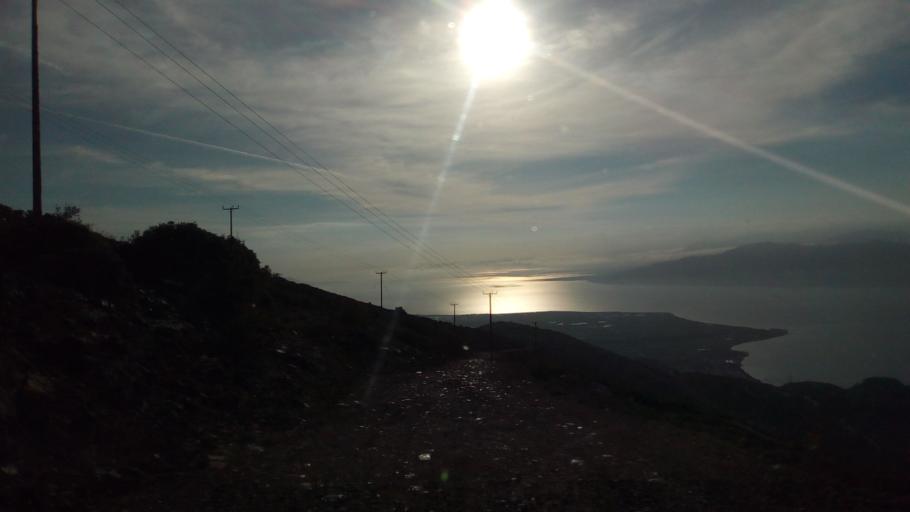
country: GR
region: West Greece
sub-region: Nomos Aitolias kai Akarnanias
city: Nafpaktos
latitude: 38.4193
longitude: 21.8051
